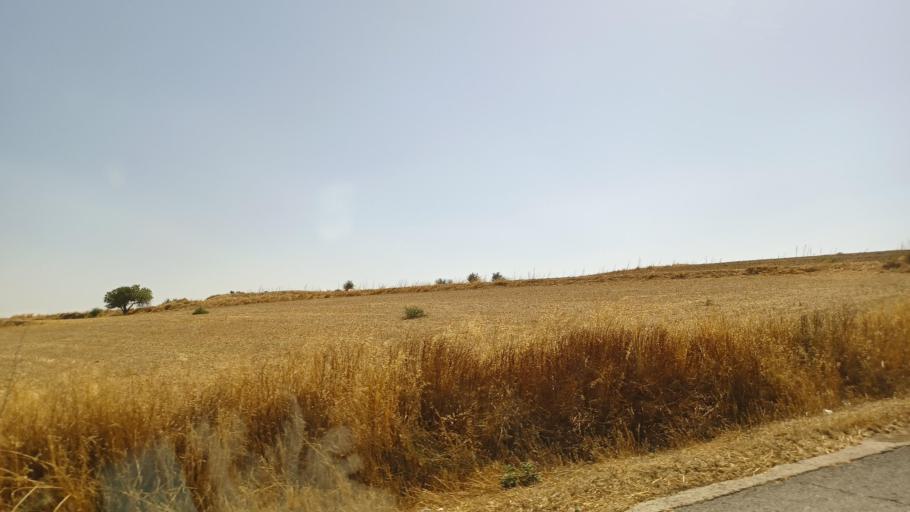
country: CY
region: Larnaka
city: Athienou
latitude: 35.0488
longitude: 33.5517
